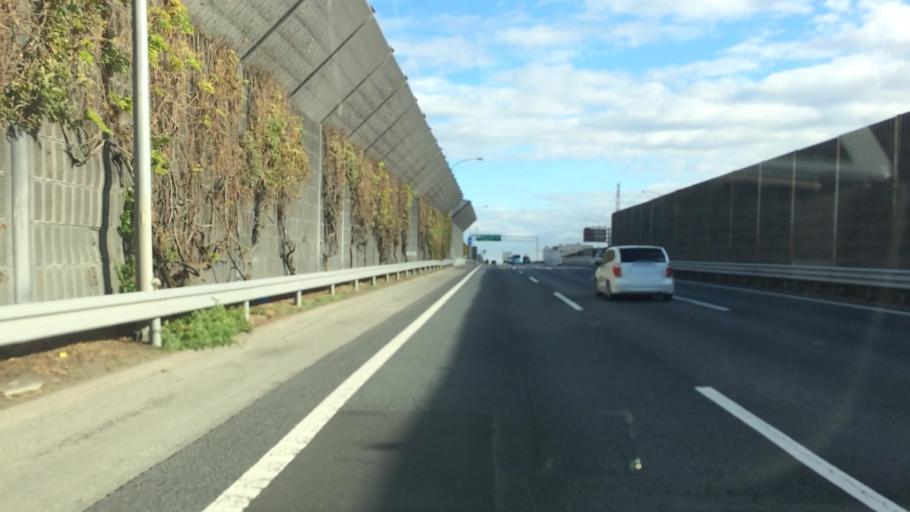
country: JP
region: Chiba
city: Chiba
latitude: 35.6461
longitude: 140.0832
